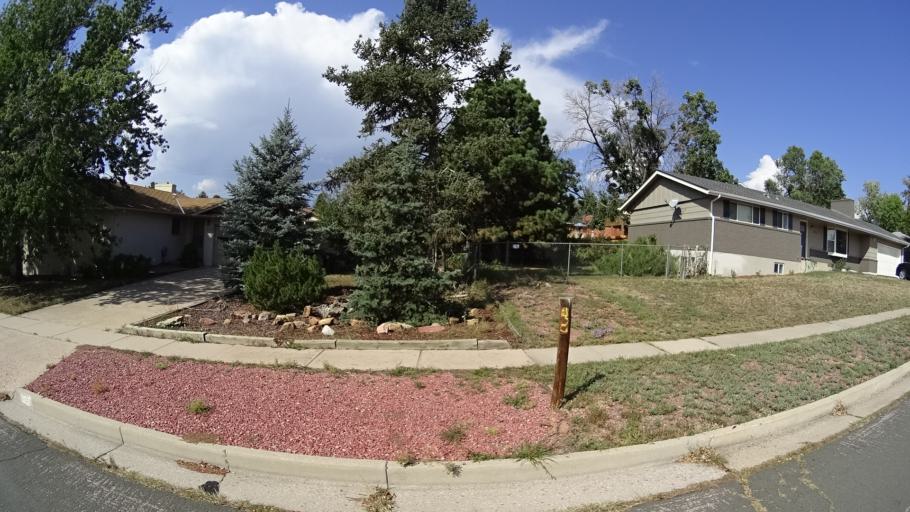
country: US
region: Colorado
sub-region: El Paso County
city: Cimarron Hills
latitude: 38.8638
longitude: -104.7596
